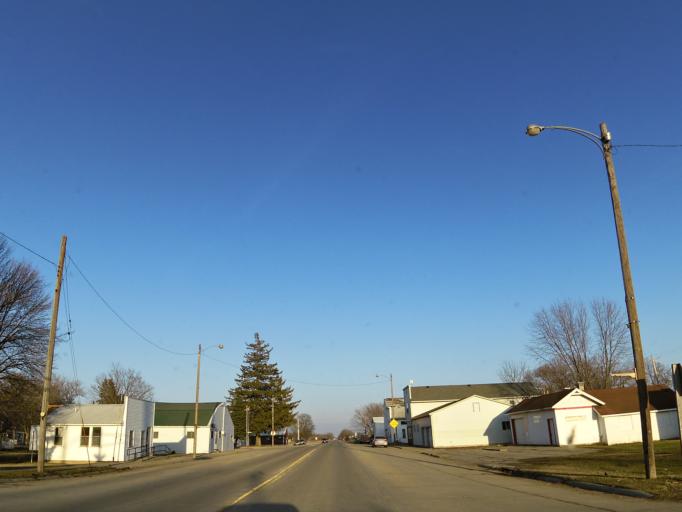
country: US
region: Iowa
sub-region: Mitchell County
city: Saint Ansgar
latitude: 43.4150
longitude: -93.0172
